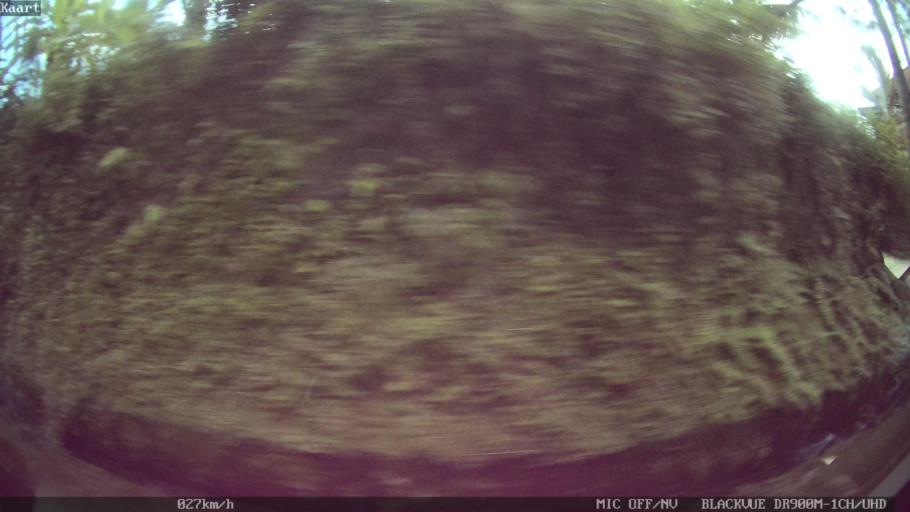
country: ID
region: Bali
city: Banjar Pesalakan
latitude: -8.5078
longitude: 115.3020
